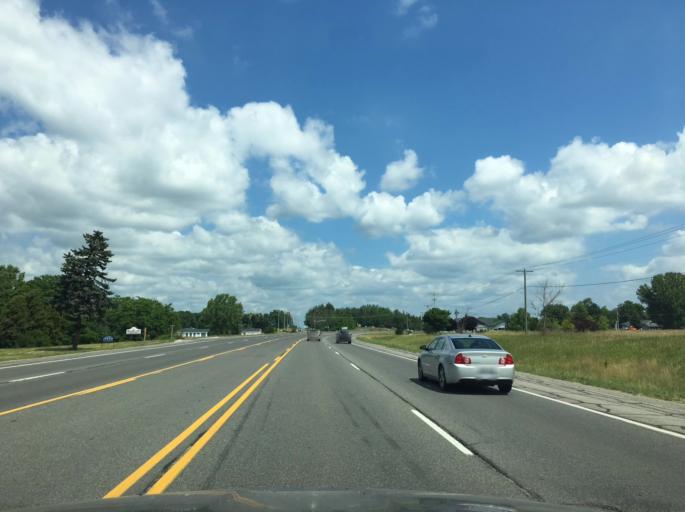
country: US
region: Michigan
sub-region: Grand Traverse County
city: Traverse City
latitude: 44.6979
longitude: -85.6563
